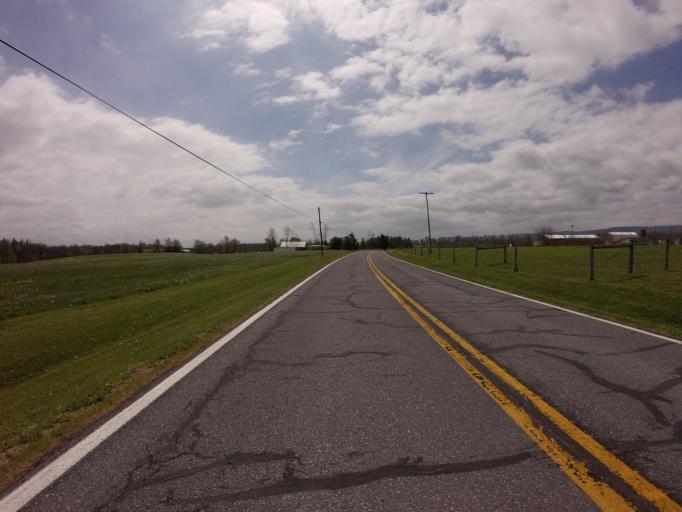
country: US
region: Maryland
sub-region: Frederick County
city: Thurmont
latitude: 39.6324
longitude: -77.3474
